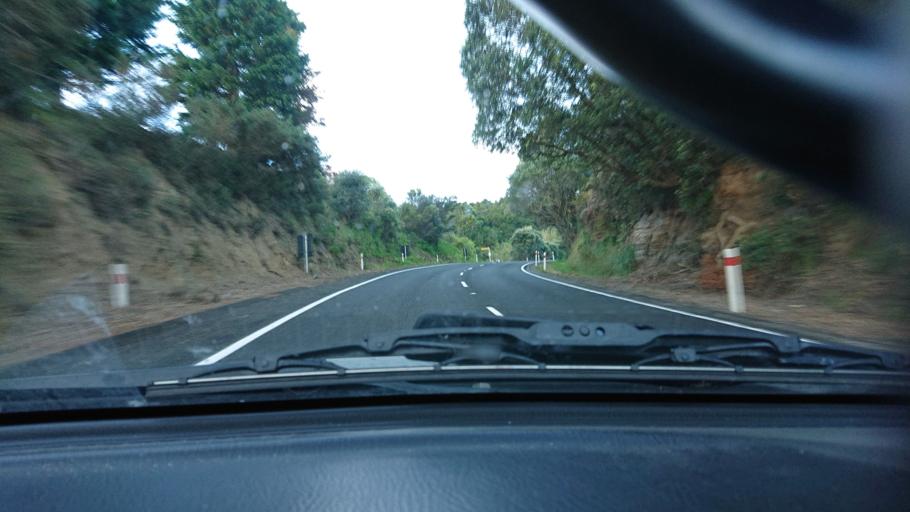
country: NZ
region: Auckland
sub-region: Auckland
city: Wellsford
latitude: -36.4381
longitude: 174.4323
